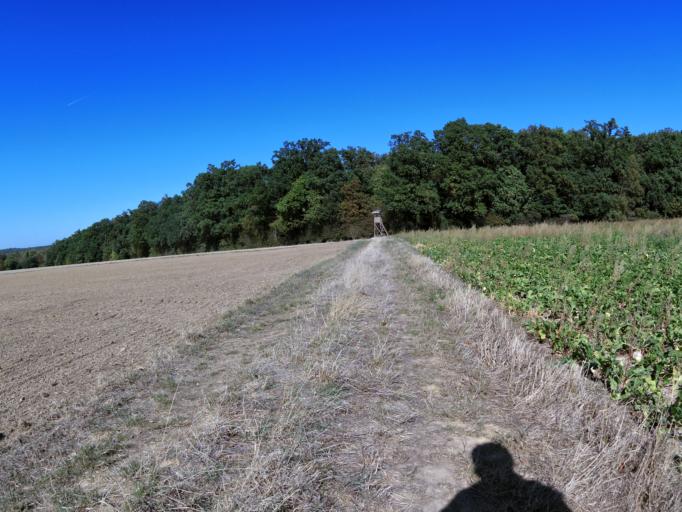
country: DE
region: Bavaria
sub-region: Regierungsbezirk Unterfranken
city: Reichenberg
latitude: 49.7346
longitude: 9.9317
